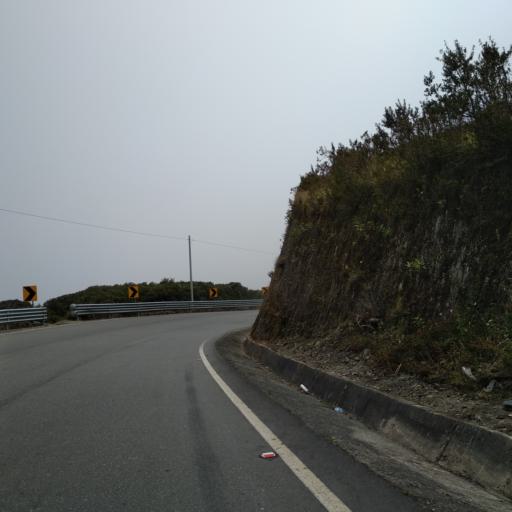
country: EC
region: Cotopaxi
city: La Mana
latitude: -0.9886
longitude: -78.9677
